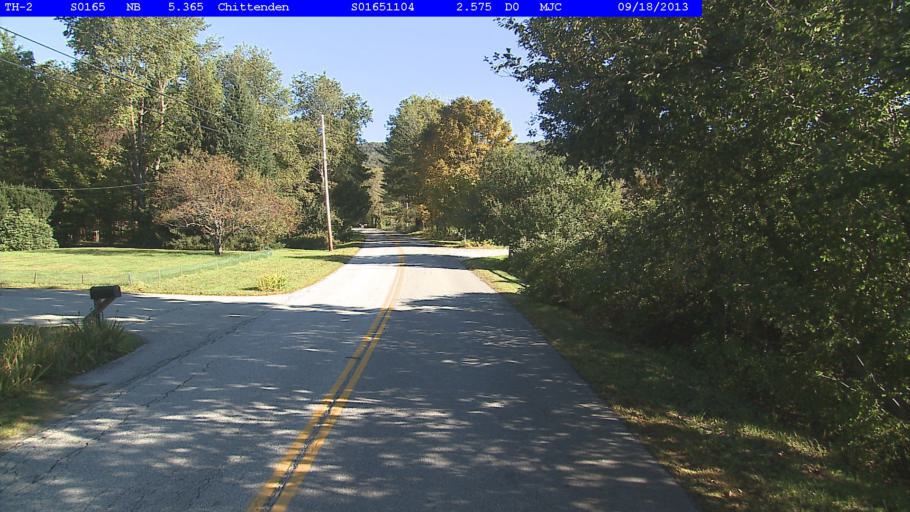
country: US
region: Vermont
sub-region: Rutland County
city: Rutland
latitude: 43.7127
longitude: -72.9614
